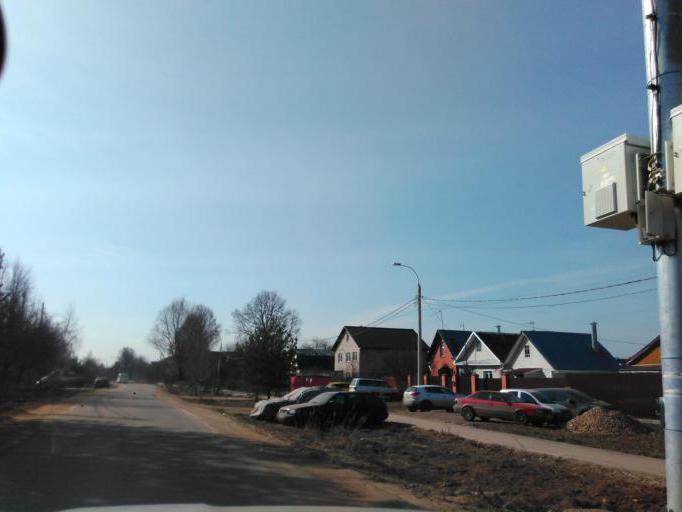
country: RU
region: Moskovskaya
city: Opalikha
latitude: 55.8818
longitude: 37.2642
